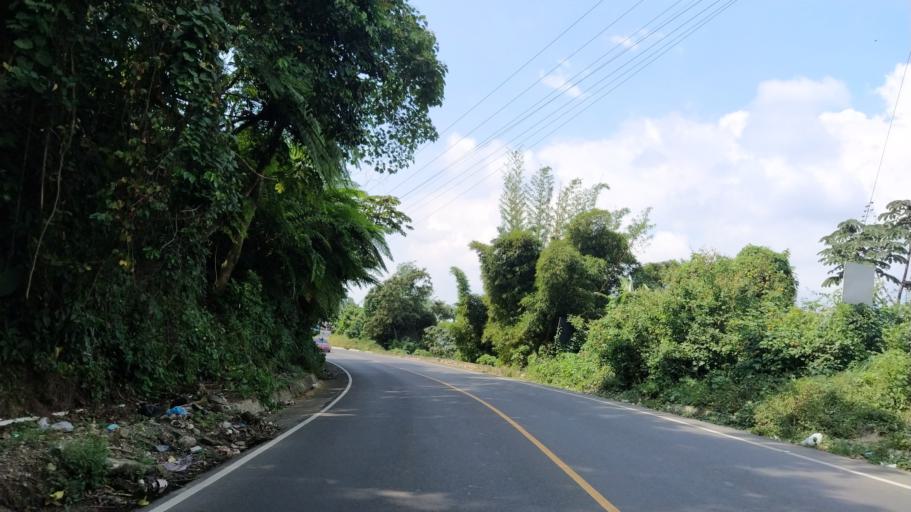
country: GT
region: Quetzaltenango
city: El Palmar
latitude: 14.6486
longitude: -91.5673
